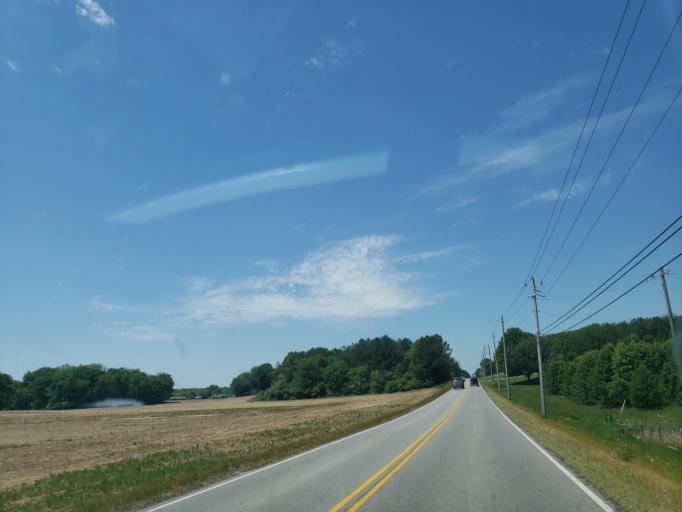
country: US
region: Alabama
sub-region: Madison County
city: Hazel Green
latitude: 34.9322
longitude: -86.5468
